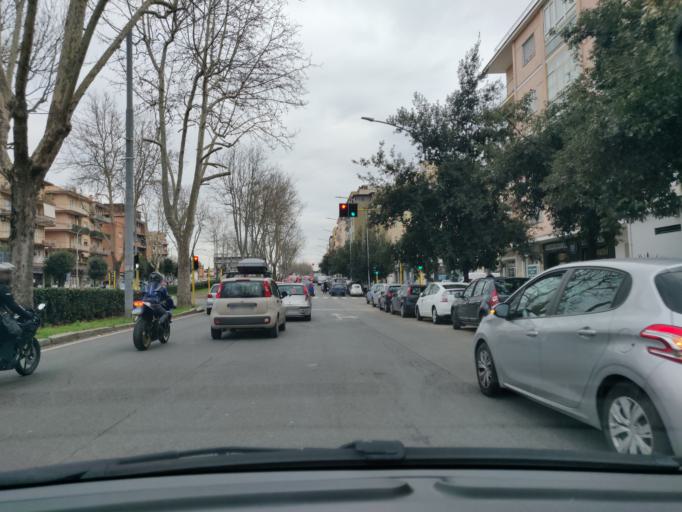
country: VA
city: Vatican City
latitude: 41.8761
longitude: 12.4445
